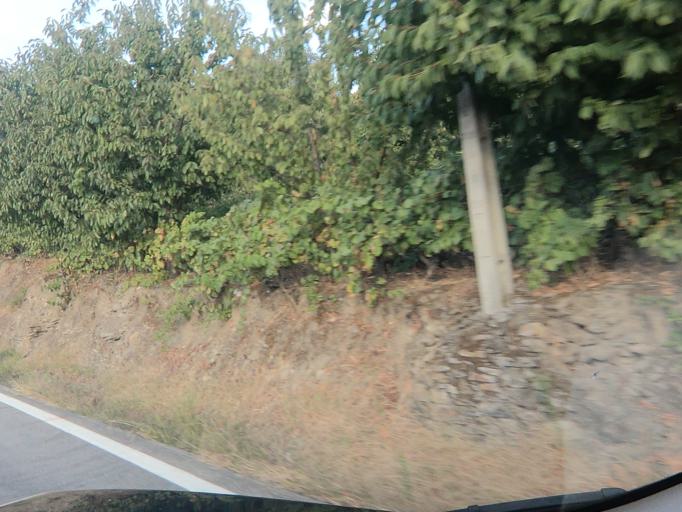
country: PT
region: Vila Real
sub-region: Peso da Regua
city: Peso da Regua
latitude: 41.1806
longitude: -7.7757
